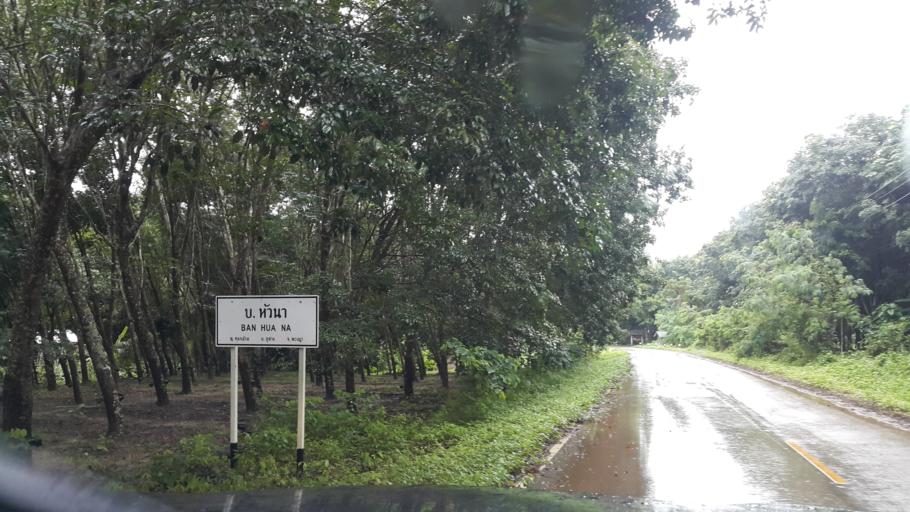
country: TH
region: Phayao
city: Phu Sang
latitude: 19.6169
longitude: 100.4059
